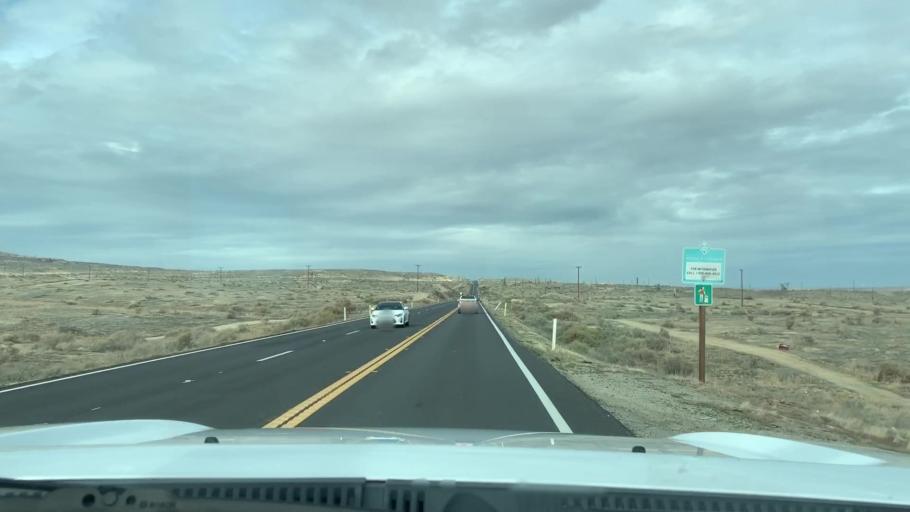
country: US
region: California
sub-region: Kern County
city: South Taft
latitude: 35.1062
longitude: -119.4208
